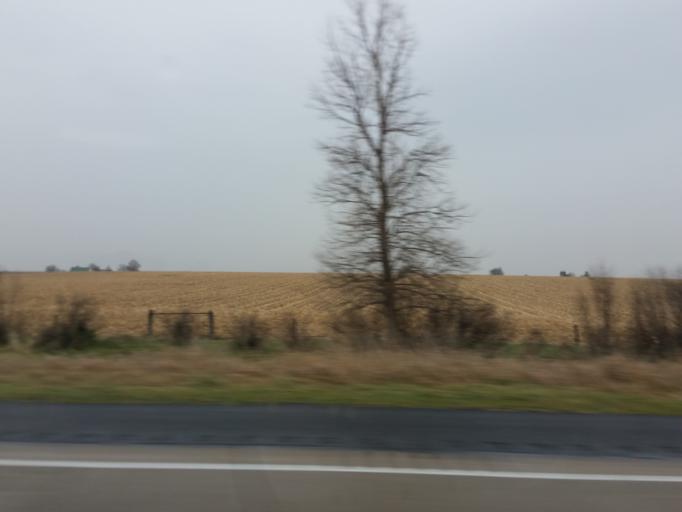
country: US
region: Iowa
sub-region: Muscatine County
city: Wilton
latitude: 41.6337
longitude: -90.9706
